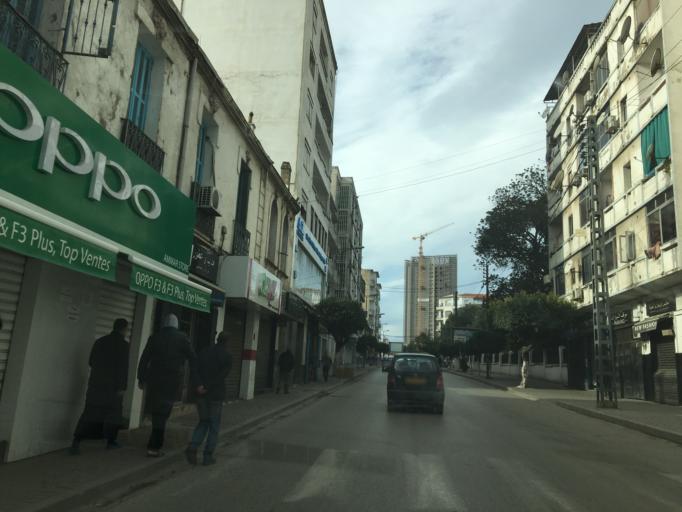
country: DZ
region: Alger
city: Algiers
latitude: 36.7692
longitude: 3.0264
